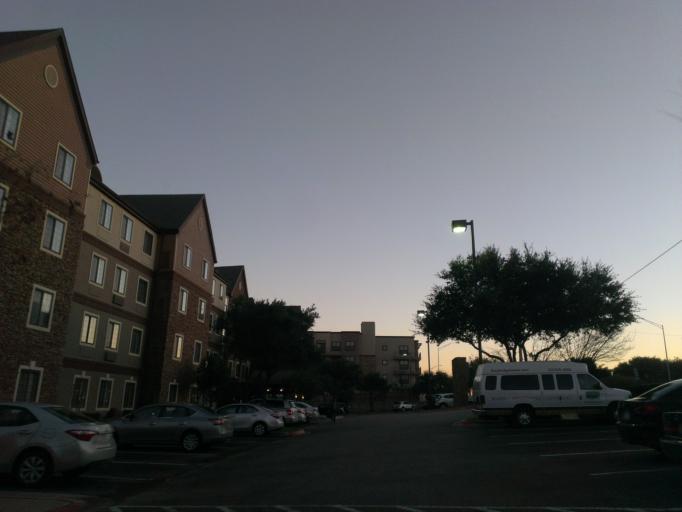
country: US
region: Texas
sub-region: Williamson County
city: Jollyville
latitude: 30.3938
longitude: -97.7394
